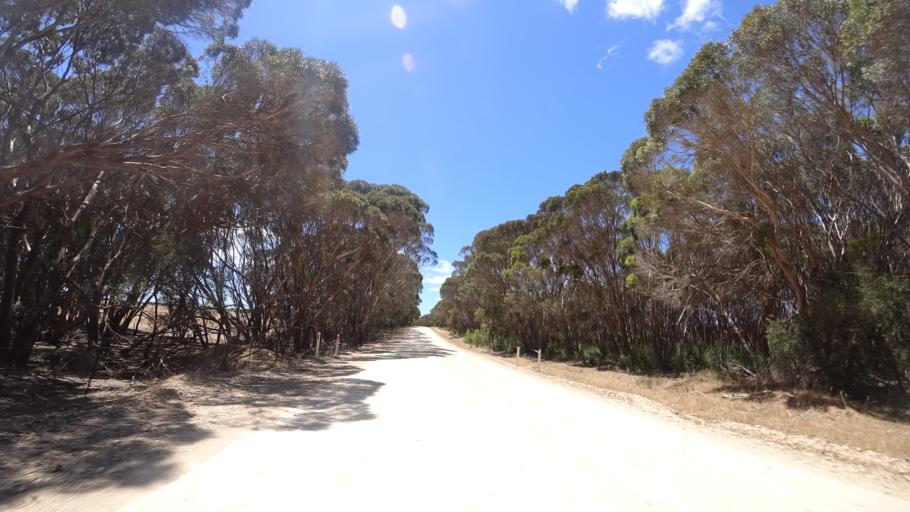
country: AU
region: South Australia
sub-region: Kangaroo Island
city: Kingscote
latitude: -35.8269
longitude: 137.9876
